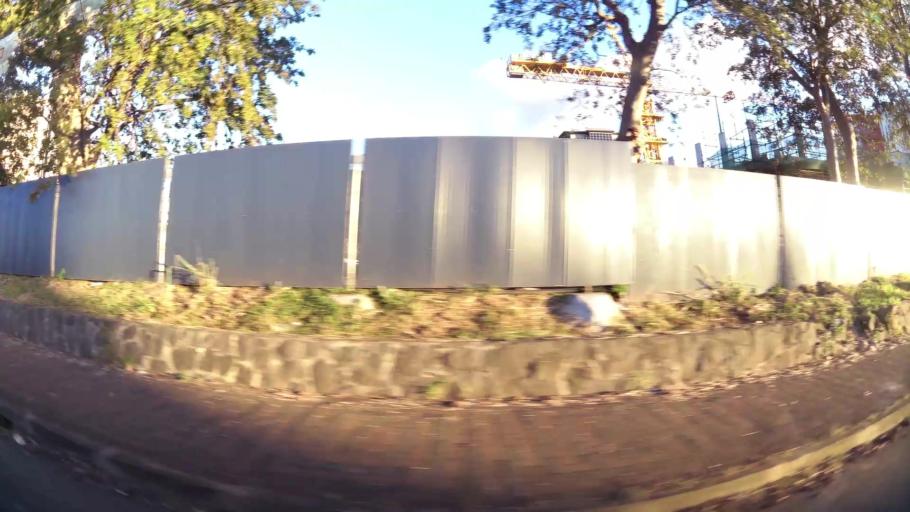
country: MU
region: Plaines Wilhems
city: Ebene
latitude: -20.2421
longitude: 57.4912
